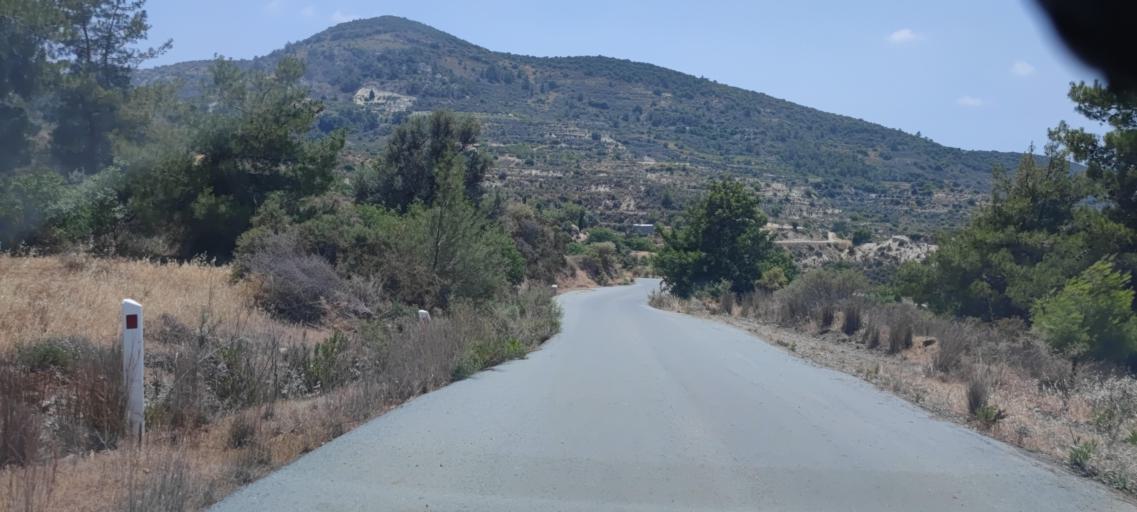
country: CY
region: Limassol
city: Pano Polemidia
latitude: 34.7970
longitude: 33.0259
